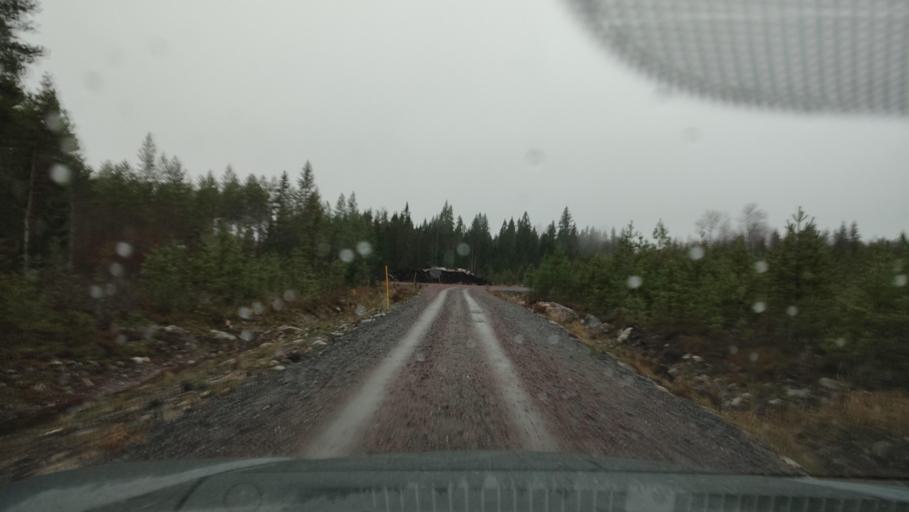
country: FI
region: Southern Ostrobothnia
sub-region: Suupohja
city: Karijoki
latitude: 62.1737
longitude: 21.7044
